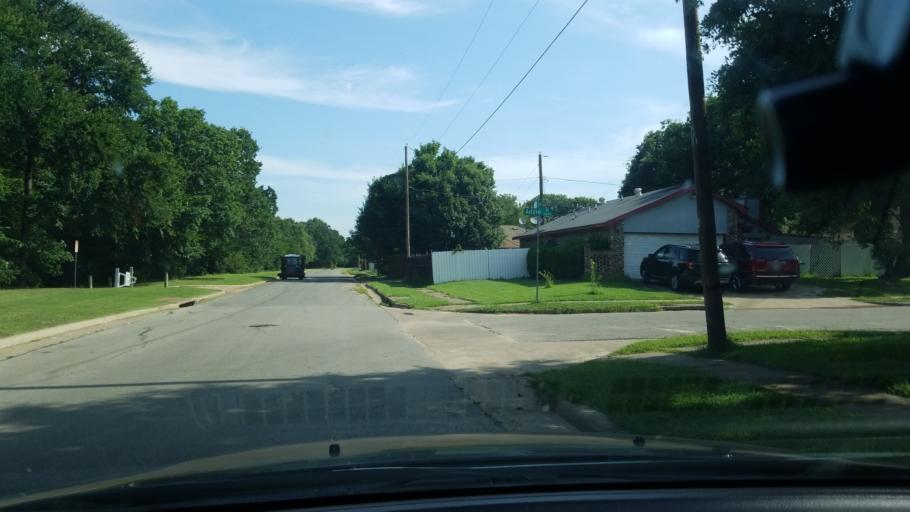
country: US
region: Texas
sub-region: Dallas County
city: Balch Springs
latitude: 32.7284
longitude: -96.6416
